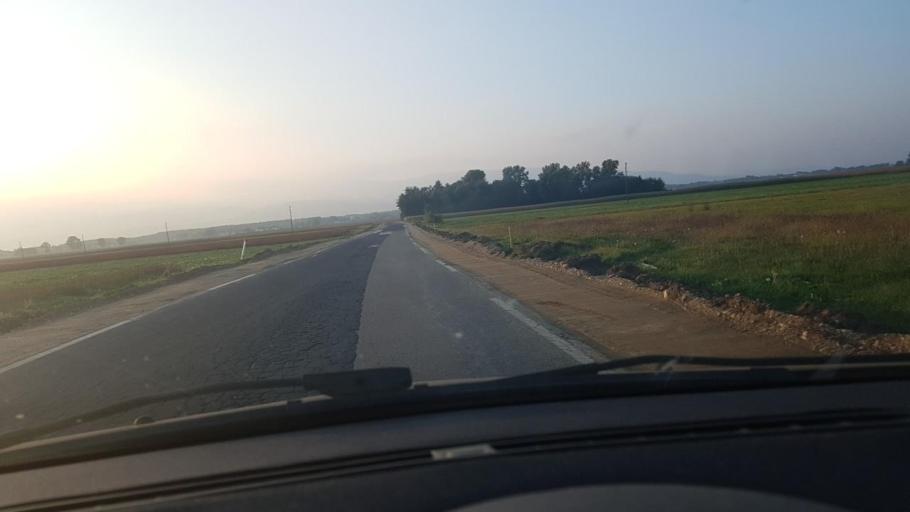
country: SI
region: Race-Fram
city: Race
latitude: 46.4098
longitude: 15.7100
